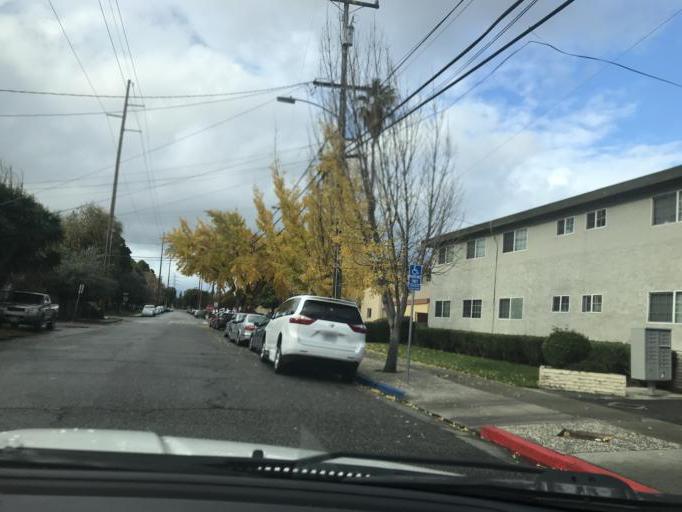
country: US
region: California
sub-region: Santa Clara County
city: Buena Vista
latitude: 37.3128
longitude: -121.9118
